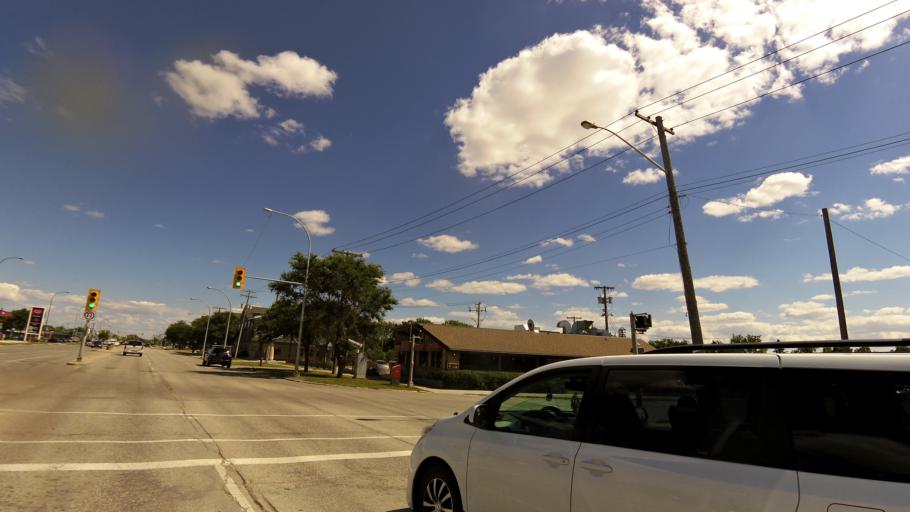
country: CA
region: Manitoba
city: Headingley
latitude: 49.8811
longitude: -97.3205
